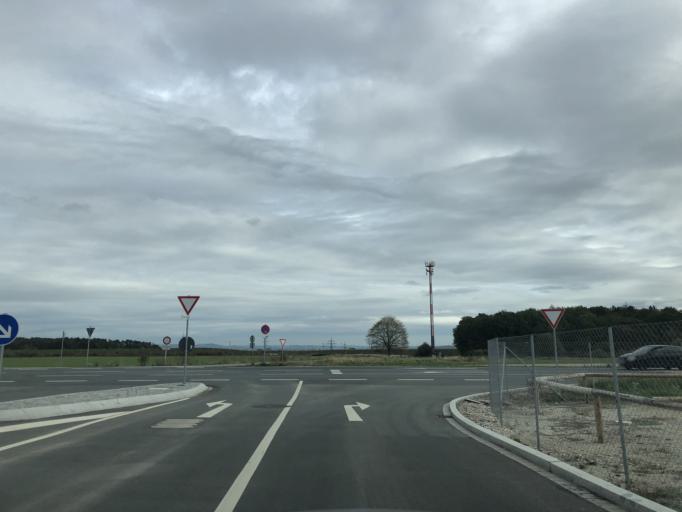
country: DE
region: Bavaria
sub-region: Regierungsbezirk Mittelfranken
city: Herzogenaurach
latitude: 49.5802
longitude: 10.9218
